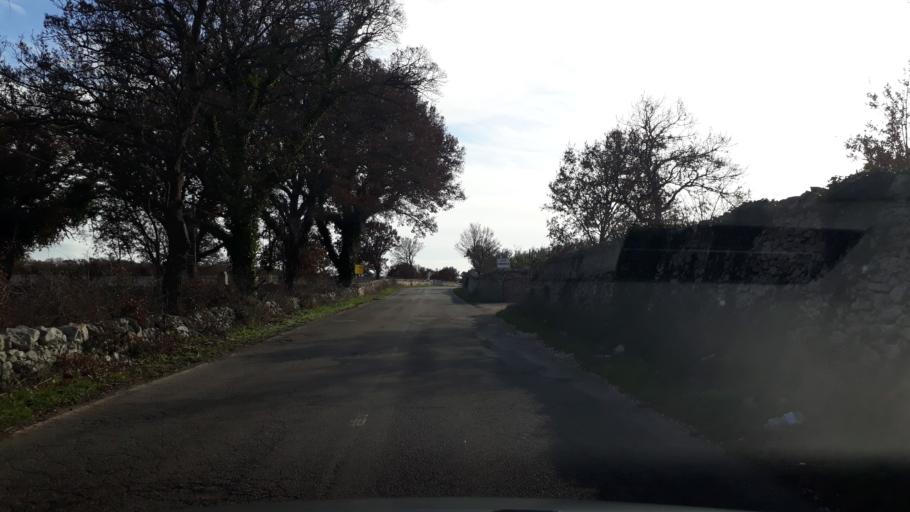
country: IT
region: Apulia
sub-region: Provincia di Taranto
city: Martina Franca
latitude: 40.6762
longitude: 17.3608
